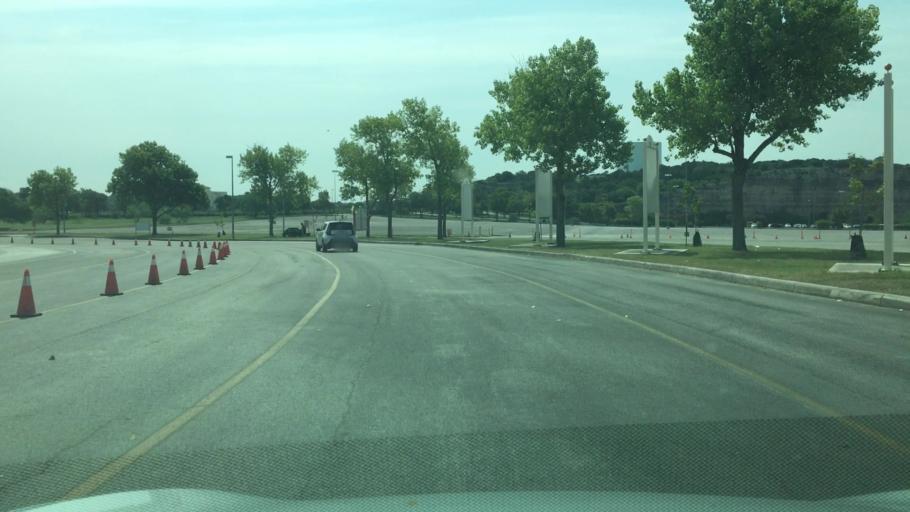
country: US
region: Texas
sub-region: Bexar County
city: Shavano Park
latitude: 29.6036
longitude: -98.6075
